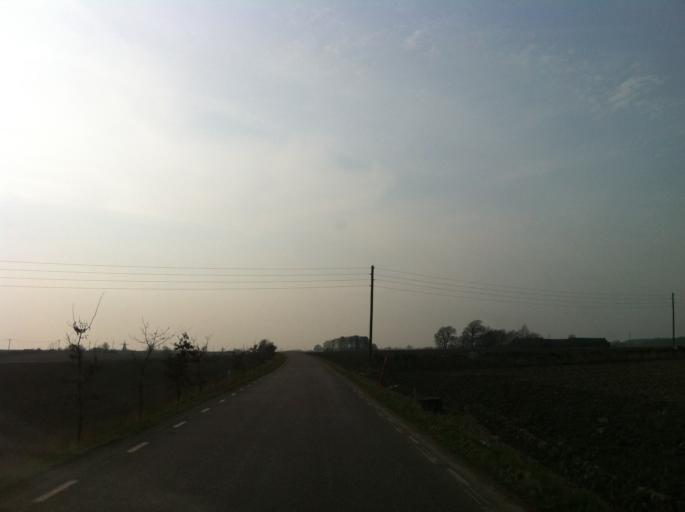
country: SE
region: Skane
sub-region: Eslovs Kommun
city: Eslov
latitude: 55.9183
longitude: 13.2443
